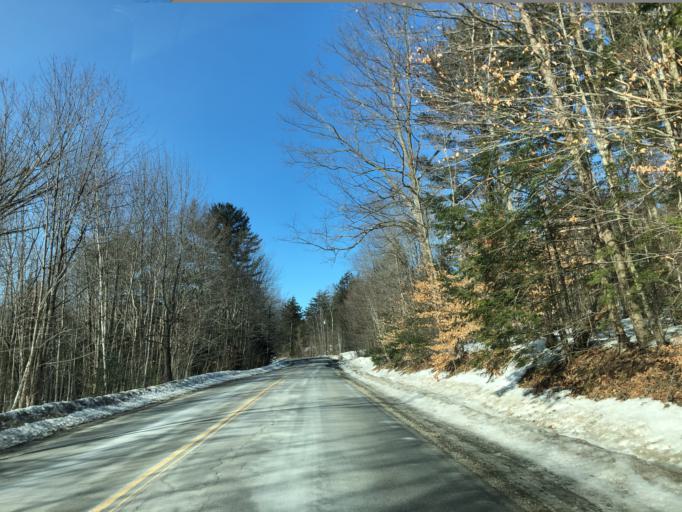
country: US
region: Maine
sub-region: Androscoggin County
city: Minot
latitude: 44.1469
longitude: -70.3303
